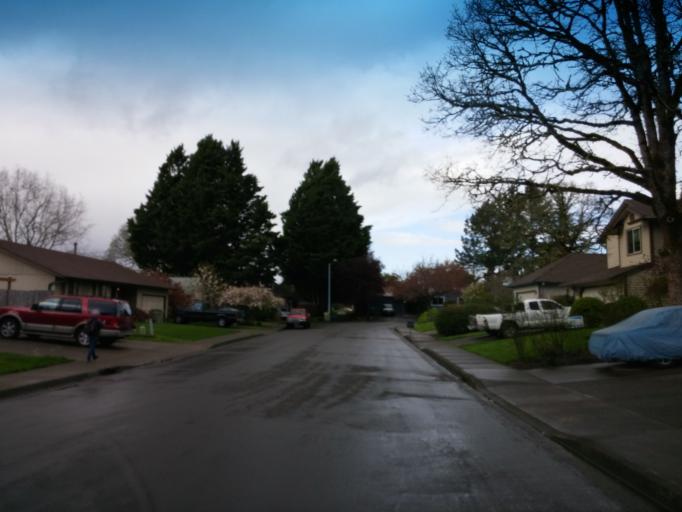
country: US
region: Oregon
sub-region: Washington County
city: Aloha
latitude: 45.5101
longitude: -122.8614
